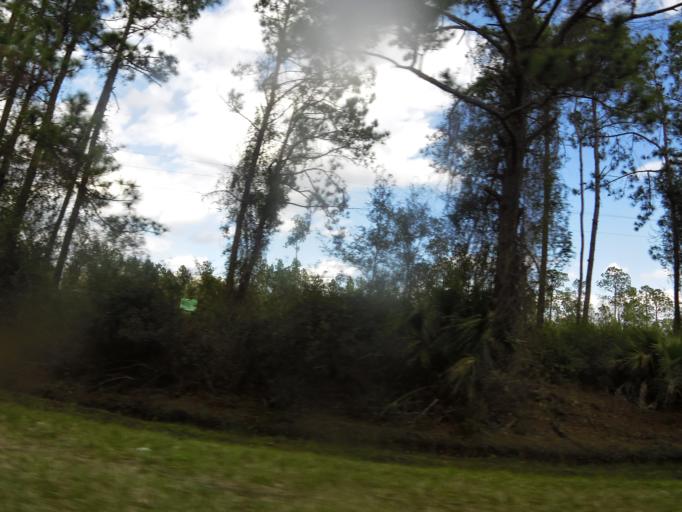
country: US
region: Florida
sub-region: Volusia County
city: De Leon Springs
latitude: 29.1787
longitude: -81.4100
